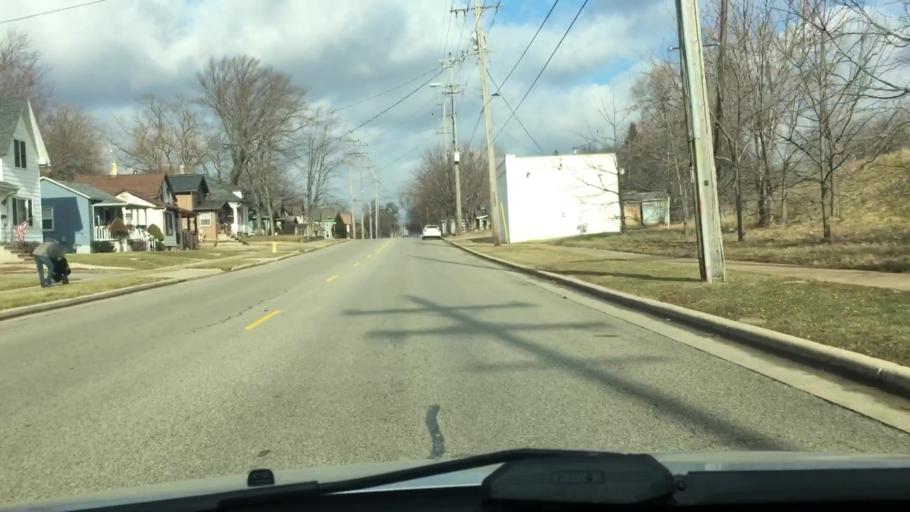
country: US
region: Wisconsin
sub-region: Waukesha County
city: Waukesha
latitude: 43.0002
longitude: -88.2368
